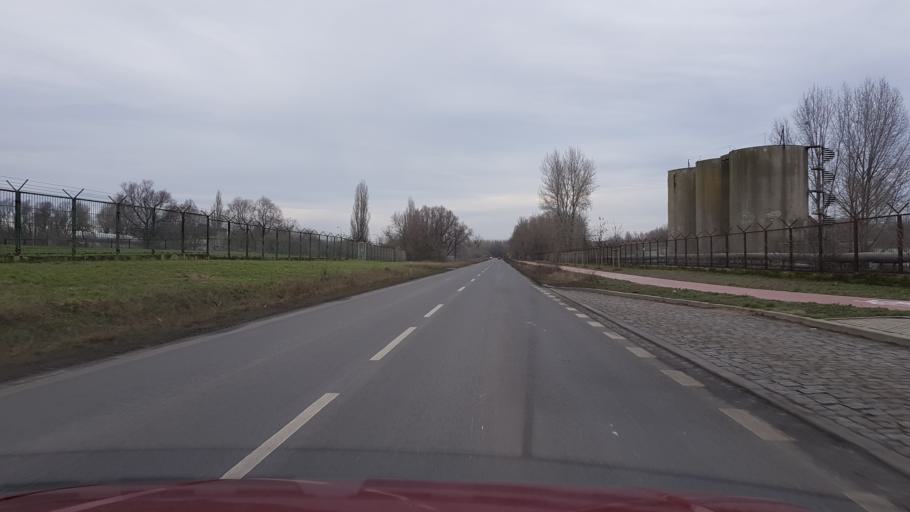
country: PL
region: West Pomeranian Voivodeship
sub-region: Powiat policki
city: Police
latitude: 53.5786
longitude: 14.5540
